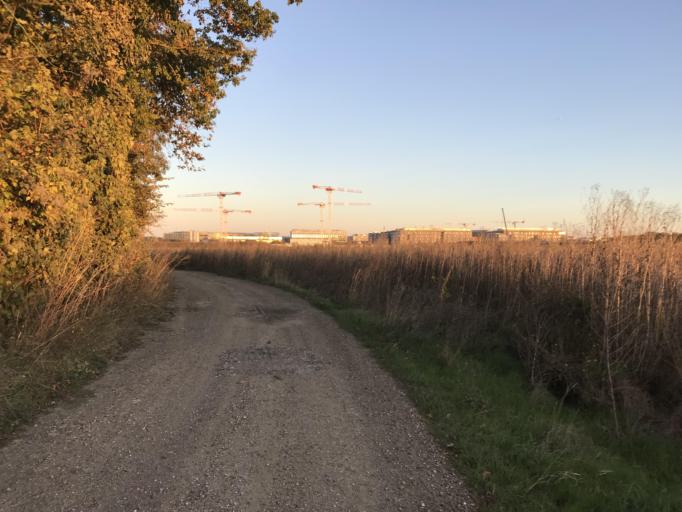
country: FR
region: Ile-de-France
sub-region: Departement de l'Essonne
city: Saclay
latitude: 48.7177
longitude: 2.1840
